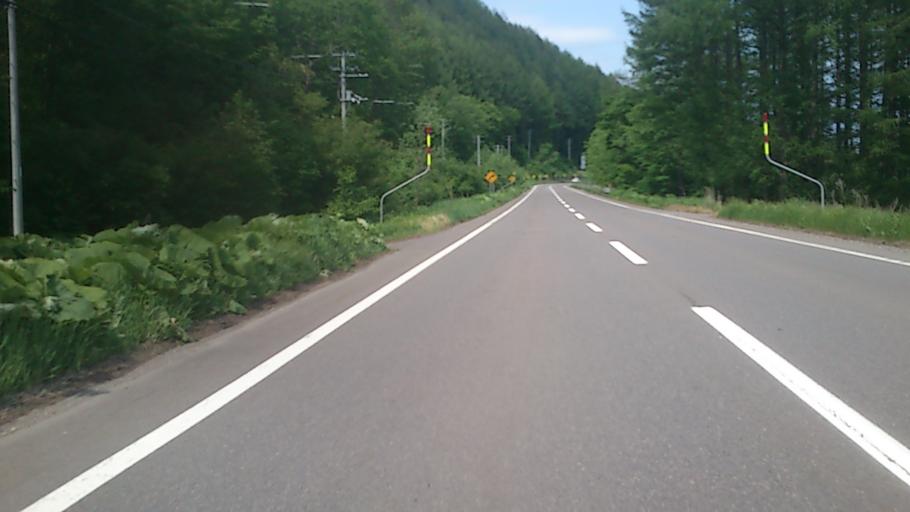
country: JP
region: Hokkaido
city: Otofuke
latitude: 43.2894
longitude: 143.6583
